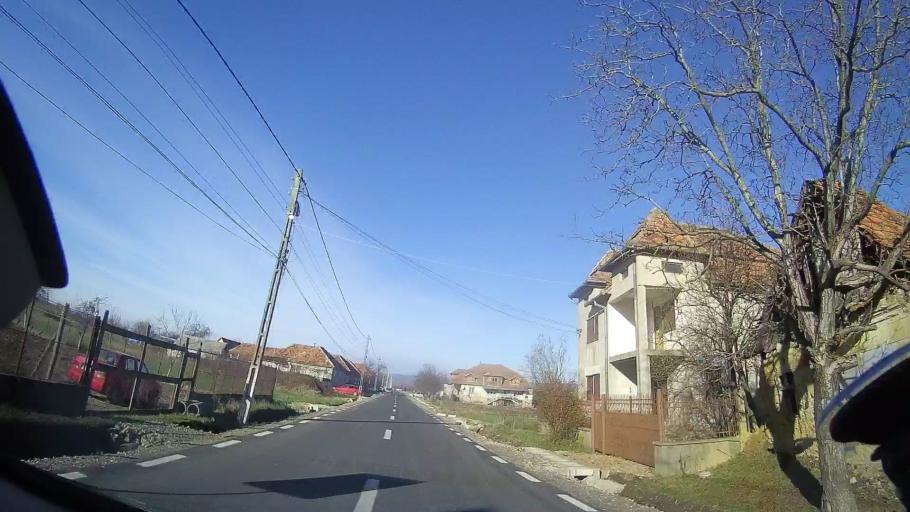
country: RO
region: Bihor
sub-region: Comuna Vadu Crisului
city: Vadu Crisului
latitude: 46.9916
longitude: 22.5091
